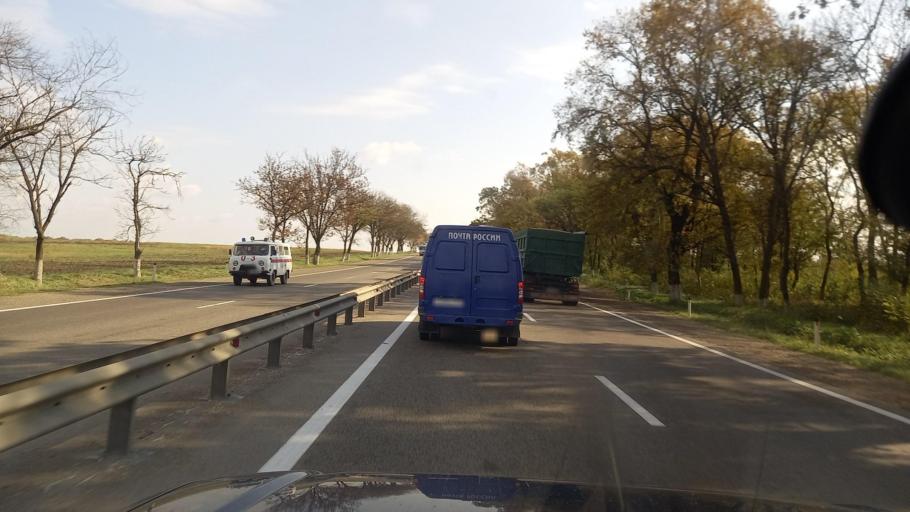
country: RU
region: Krasnodarskiy
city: Akhtyrskiy
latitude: 44.8543
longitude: 38.2525
